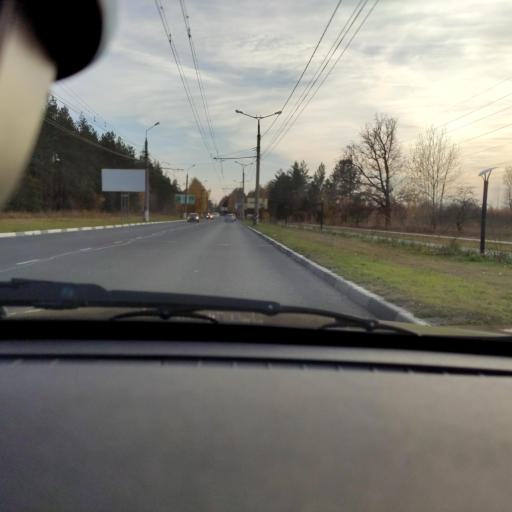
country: RU
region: Samara
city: Tol'yatti
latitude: 53.4962
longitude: 49.3878
